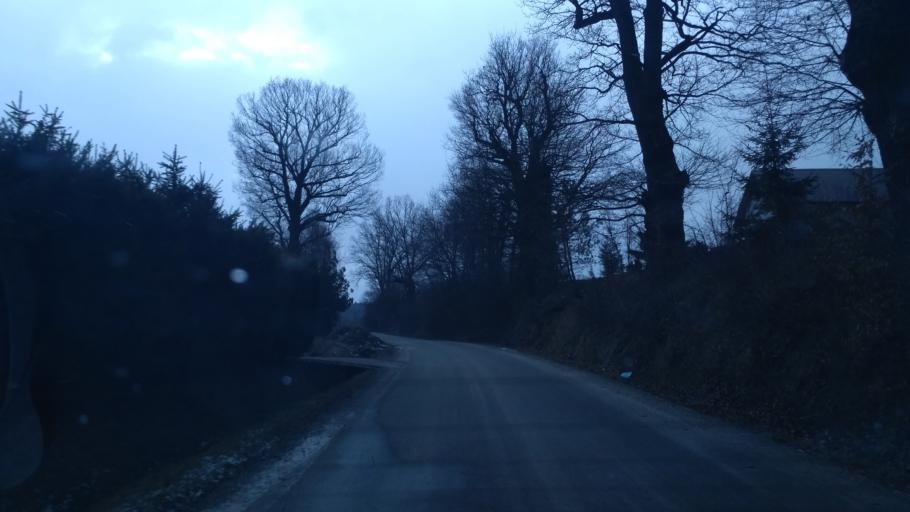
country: PL
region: Subcarpathian Voivodeship
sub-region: Powiat rzeszowski
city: Hyzne
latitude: 49.9040
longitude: 22.1963
